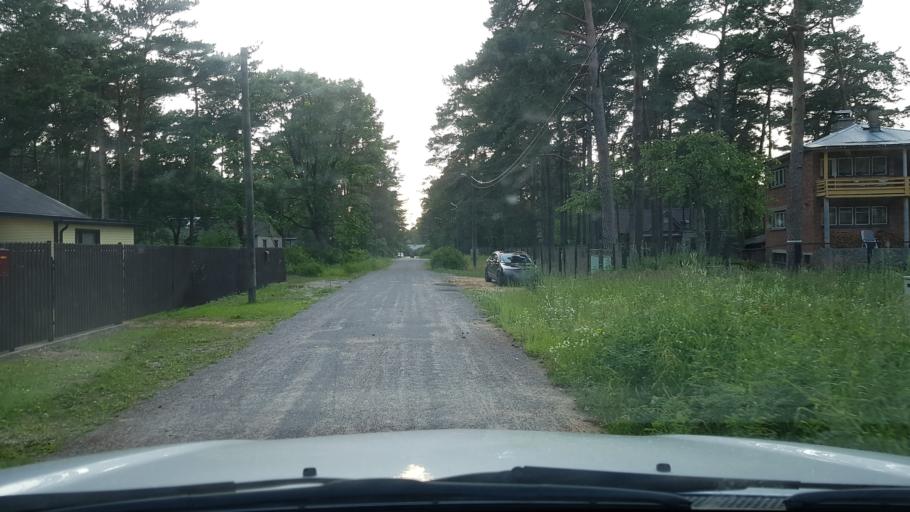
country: EE
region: Ida-Virumaa
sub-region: Narva-Joesuu linn
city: Narva-Joesuu
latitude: 59.4547
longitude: 28.0541
